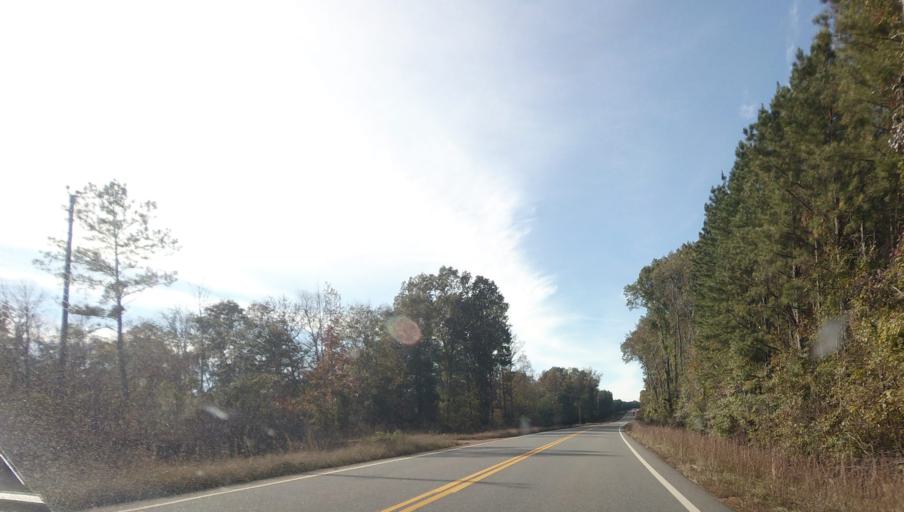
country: US
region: Georgia
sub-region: Taylor County
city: Butler
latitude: 32.7155
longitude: -84.3019
